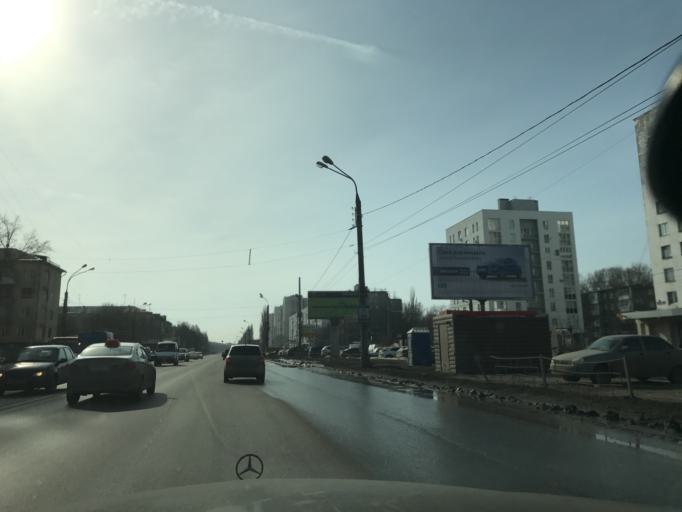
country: RU
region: Nizjnij Novgorod
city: Nizhniy Novgorod
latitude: 56.2774
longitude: 43.9220
